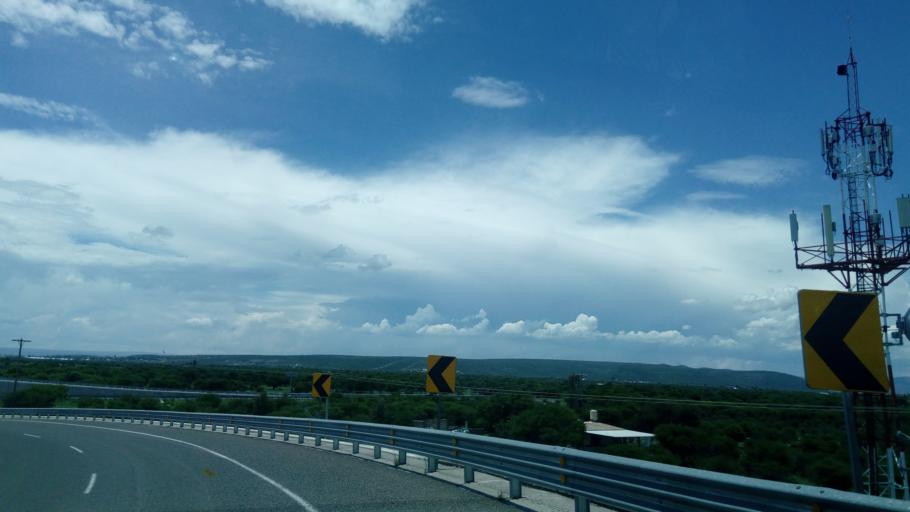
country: MX
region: Durango
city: Victoria de Durango
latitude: 24.1280
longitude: -104.5380
